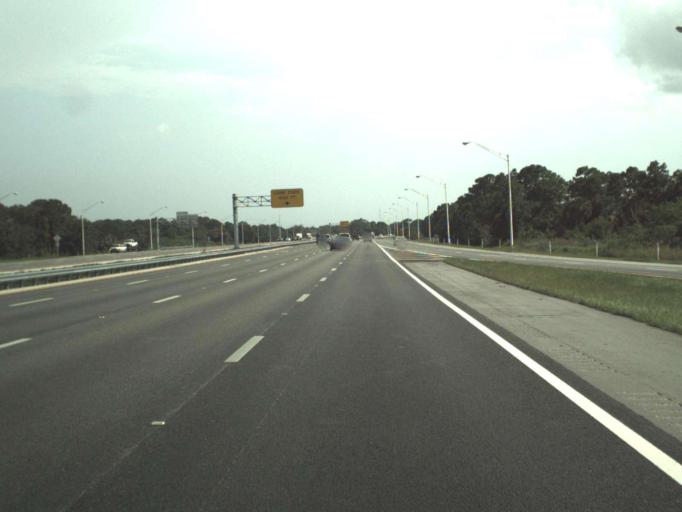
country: US
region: Florida
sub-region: Saint Lucie County
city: Fort Pierce South
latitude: 27.4122
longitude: -80.3887
